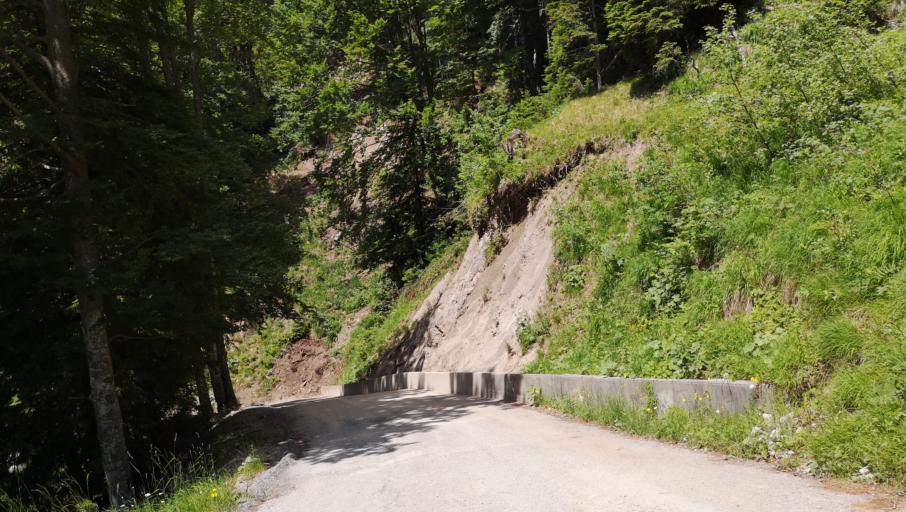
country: IT
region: Friuli Venezia Giulia
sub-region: Provincia di Udine
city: Pontebba
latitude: 46.5107
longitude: 13.2514
